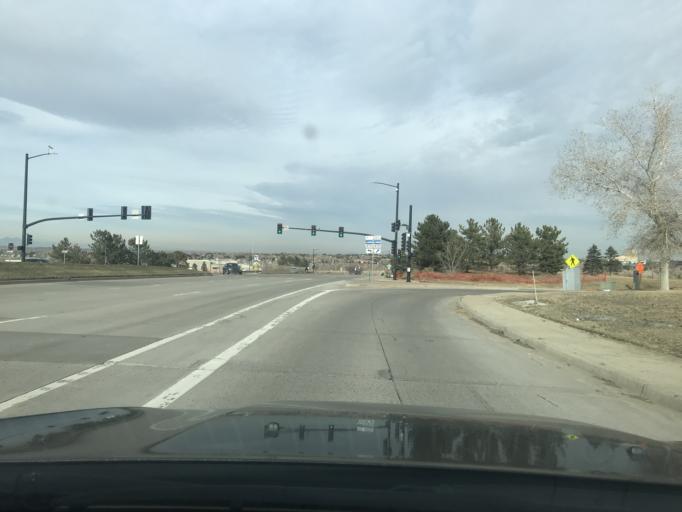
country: US
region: Colorado
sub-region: Douglas County
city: Highlands Ranch
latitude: 39.5581
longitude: -105.0080
